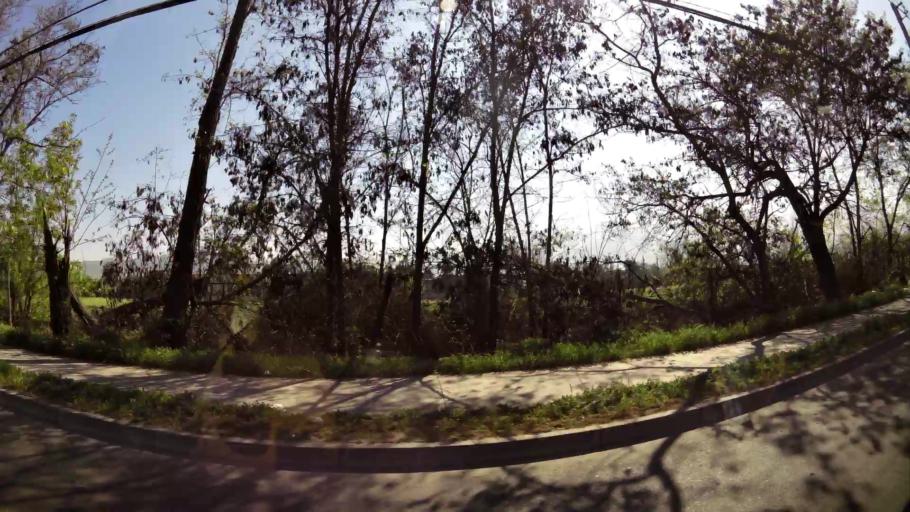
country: CL
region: Santiago Metropolitan
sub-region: Provincia de Chacabuco
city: Chicureo Abajo
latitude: -33.3678
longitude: -70.6726
